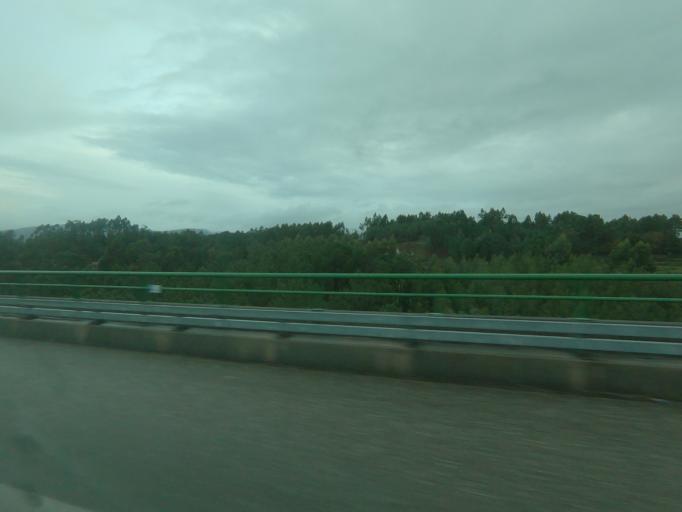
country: PT
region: Viana do Castelo
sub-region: Vila Nova de Cerveira
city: Vila Nova de Cerveira
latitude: 41.9555
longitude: -8.6726
